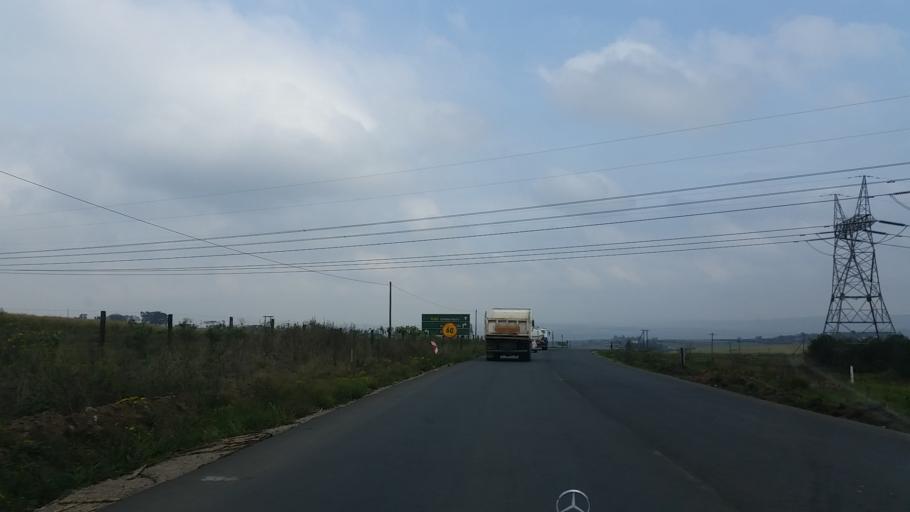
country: ZA
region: KwaZulu-Natal
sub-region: uMgungundlovu District Municipality
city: Camperdown
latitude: -29.7665
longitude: 30.5082
